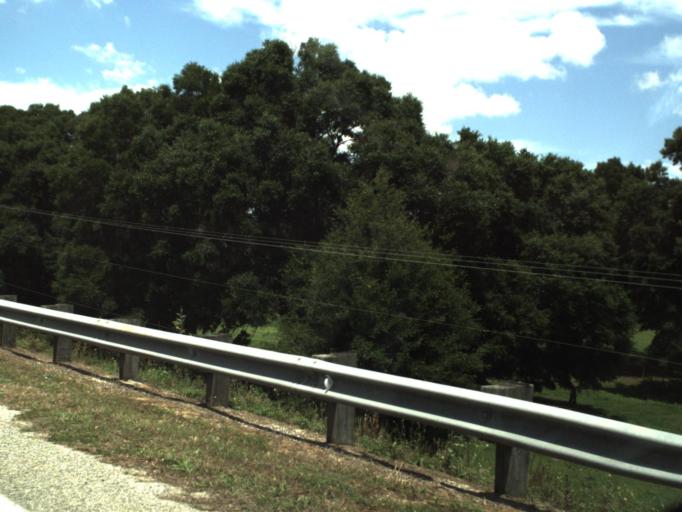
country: US
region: Florida
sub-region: Marion County
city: Citra
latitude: 29.3987
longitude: -82.2012
